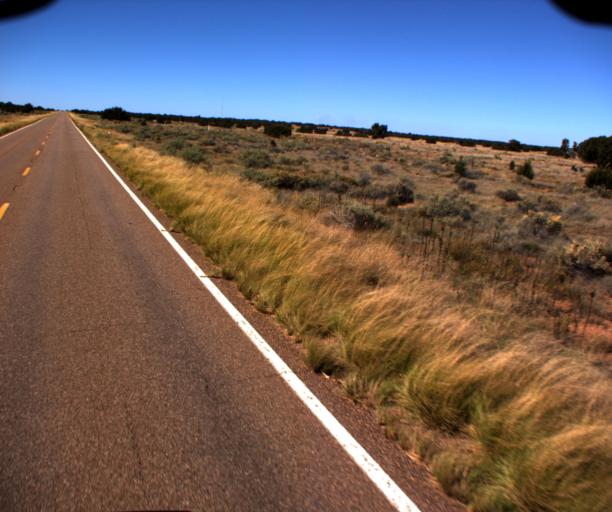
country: US
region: Arizona
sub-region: Navajo County
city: Heber-Overgaard
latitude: 34.4687
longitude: -110.3675
